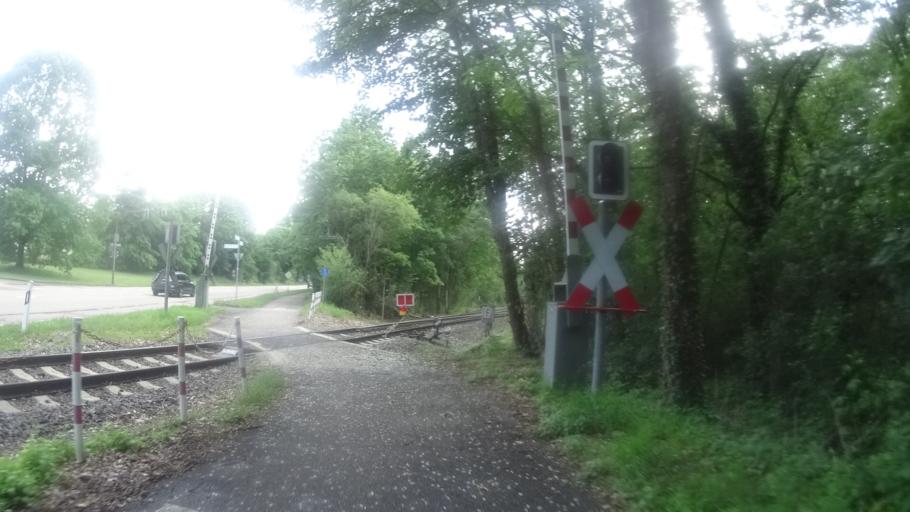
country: DE
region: Baden-Wuerttemberg
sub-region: Karlsruhe Region
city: Rastatt
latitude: 48.8387
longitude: 8.1879
